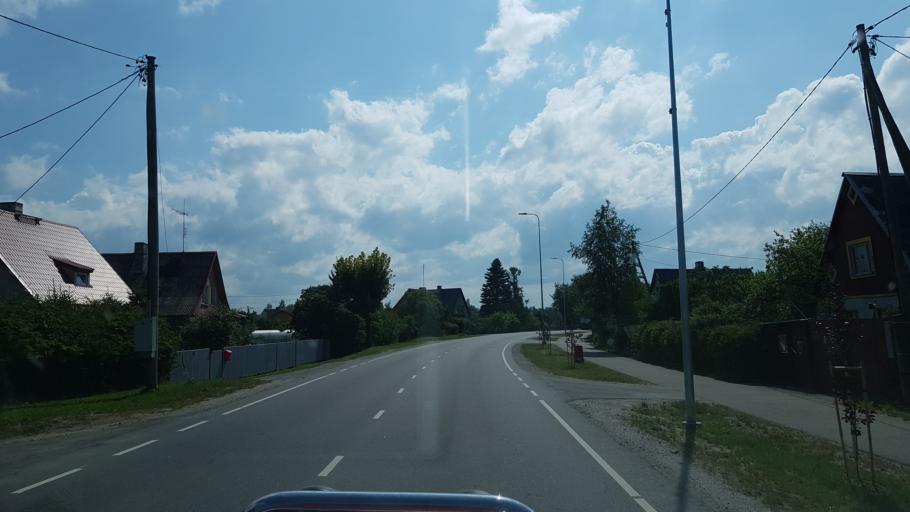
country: EE
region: Ida-Virumaa
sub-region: Kohtla-Jaerve linn
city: Kohtla-Jarve
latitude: 59.3813
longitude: 27.2576
